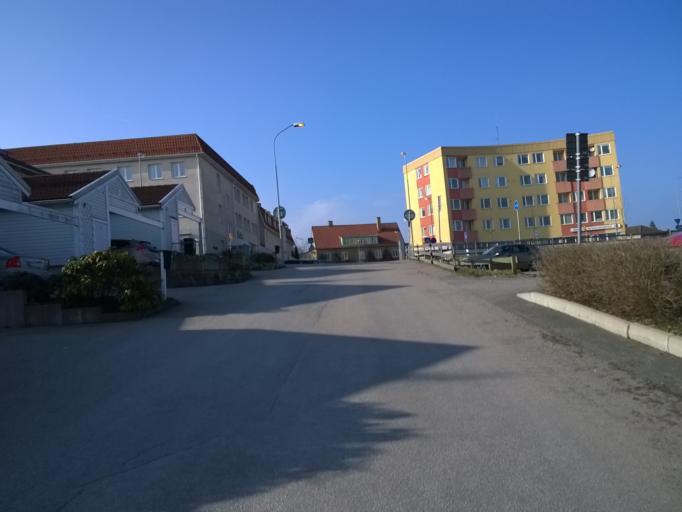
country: SE
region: Kronoberg
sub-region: Alvesta Kommun
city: Alvesta
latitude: 56.9017
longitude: 14.5586
